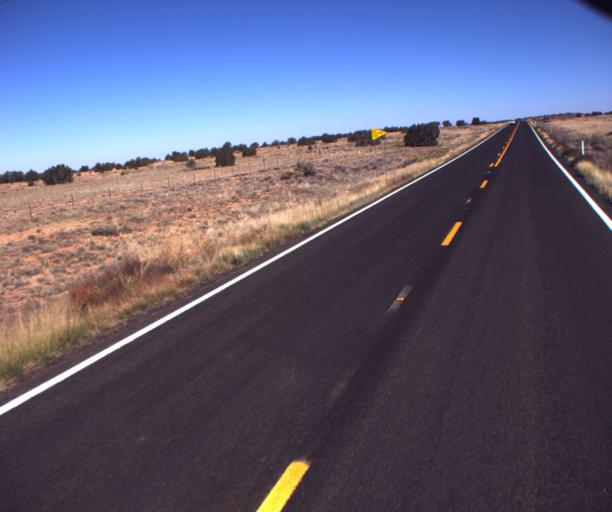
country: US
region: Arizona
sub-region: Coconino County
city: Tuba City
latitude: 35.9267
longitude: -110.8556
